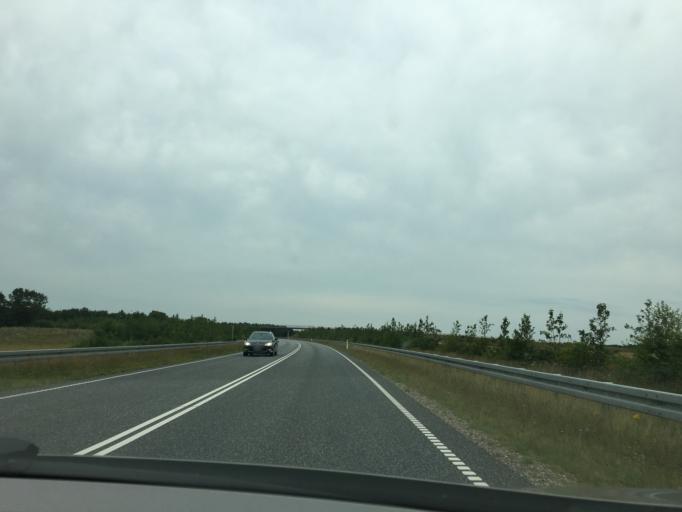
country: DK
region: Central Jutland
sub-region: Herning Kommune
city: Sunds
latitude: 56.2090
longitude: 8.9912
